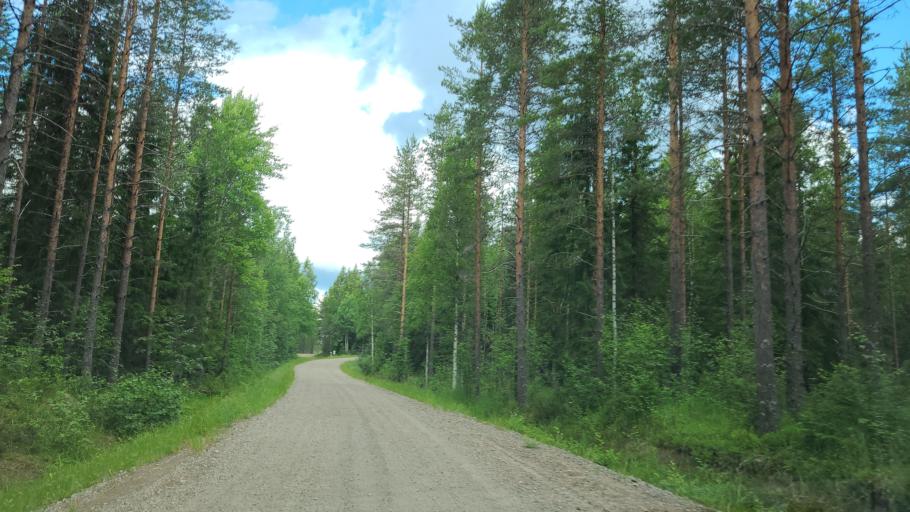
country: FI
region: Northern Savo
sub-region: Koillis-Savo
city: Kaavi
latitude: 63.0500
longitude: 28.8157
